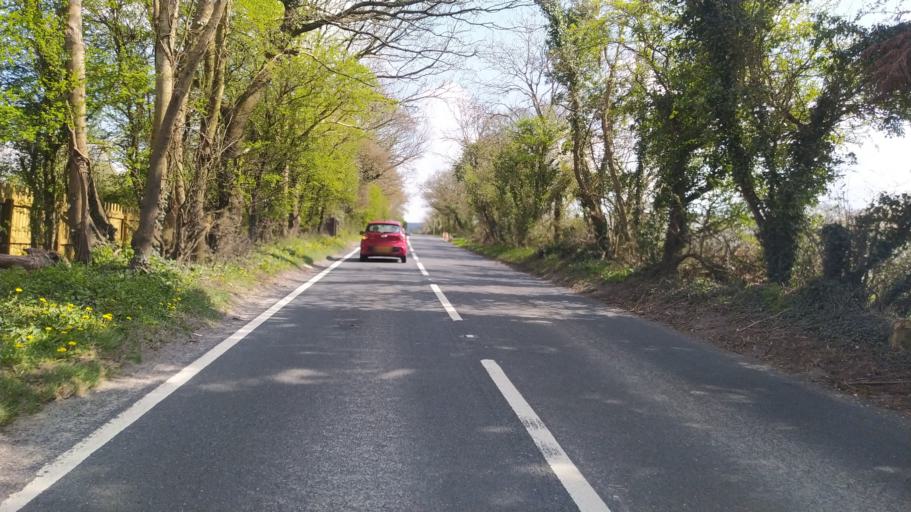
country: GB
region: England
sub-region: Wiltshire
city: Corsley
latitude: 51.2180
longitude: -2.2830
